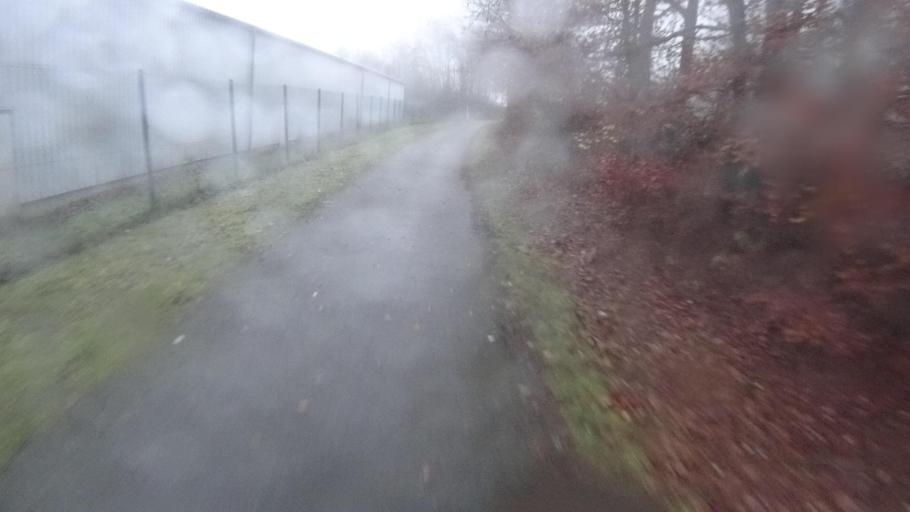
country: DE
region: Rheinland-Pfalz
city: Kratzenburg
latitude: 50.2038
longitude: 7.5669
